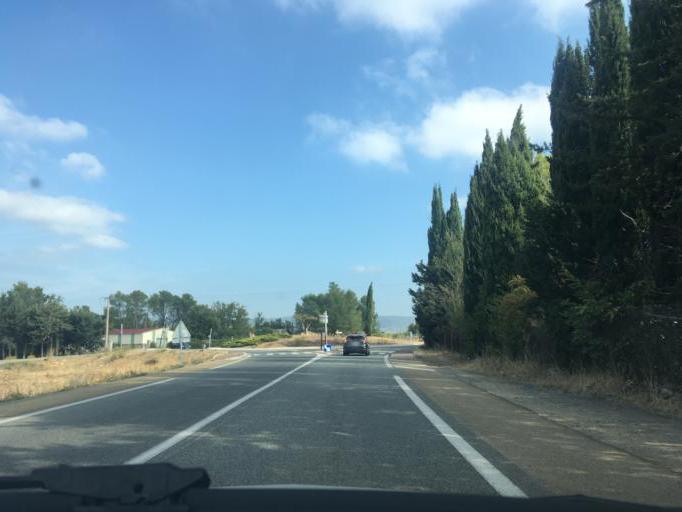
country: FR
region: Provence-Alpes-Cote d'Azur
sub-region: Departement du Var
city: Flayosc
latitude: 43.5095
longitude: 6.4251
